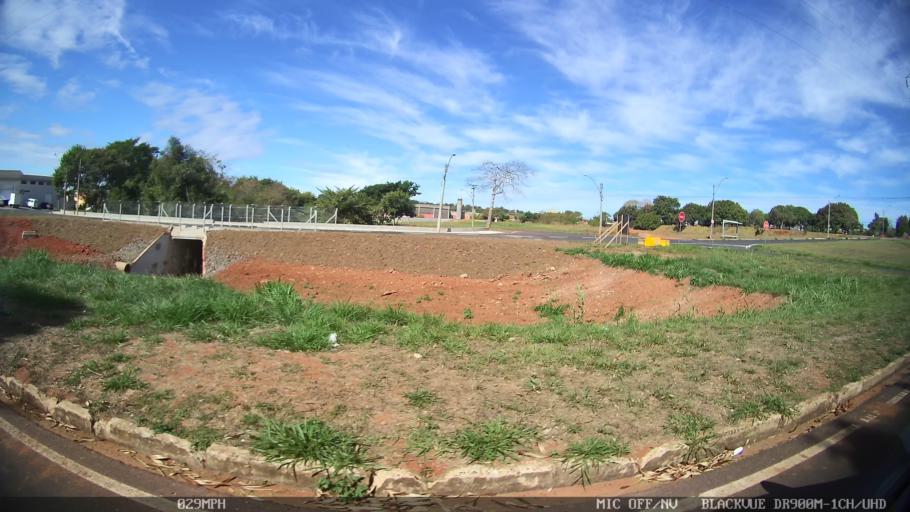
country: BR
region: Sao Paulo
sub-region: Sao Jose Do Rio Preto
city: Sao Jose do Rio Preto
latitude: -20.8428
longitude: -49.3627
